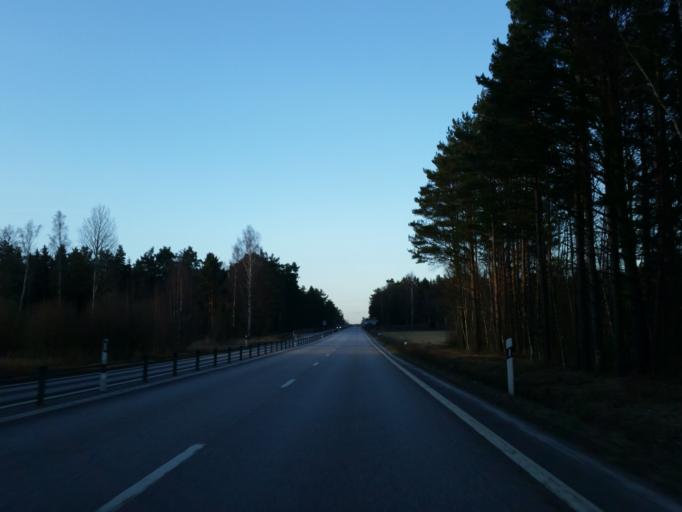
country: SE
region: Kalmar
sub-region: Oskarshamns Kommun
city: Oskarshamn
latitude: 57.3455
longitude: 16.4890
